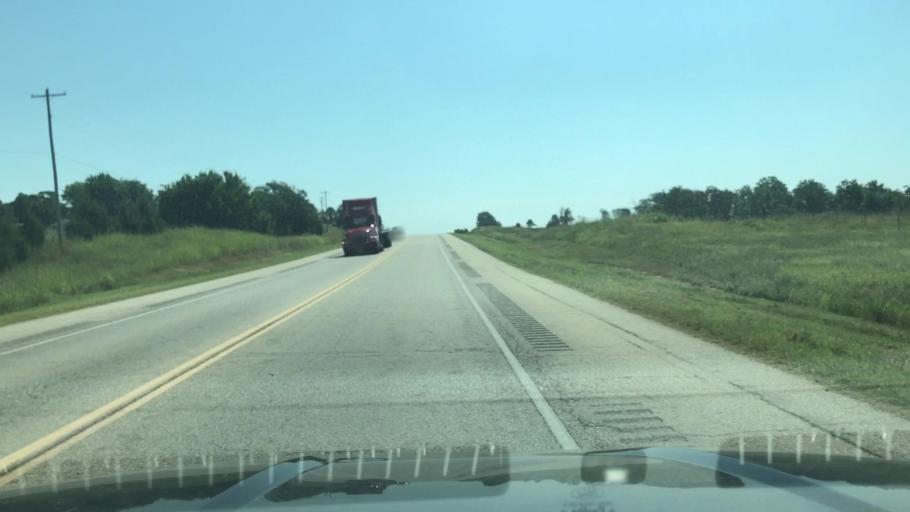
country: US
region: Oklahoma
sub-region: Creek County
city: Mannford
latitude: 36.0031
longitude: -96.4118
